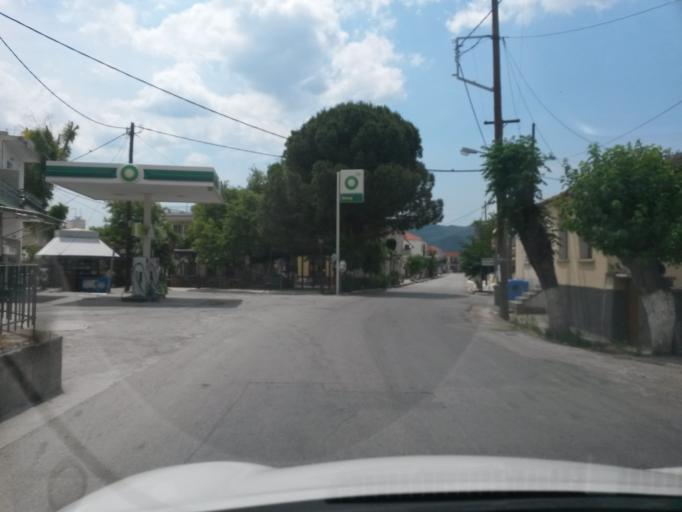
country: GR
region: North Aegean
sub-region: Nomos Lesvou
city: Kalloni
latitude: 39.2304
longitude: 26.2178
